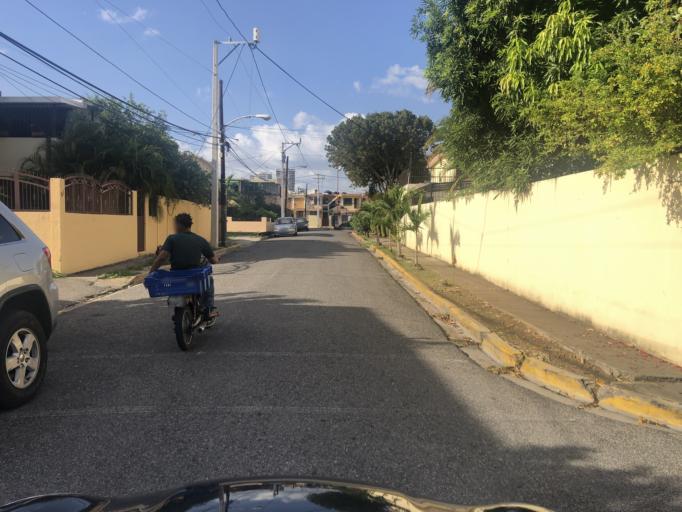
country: DO
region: Nacional
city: La Julia
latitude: 18.4526
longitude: -69.9266
